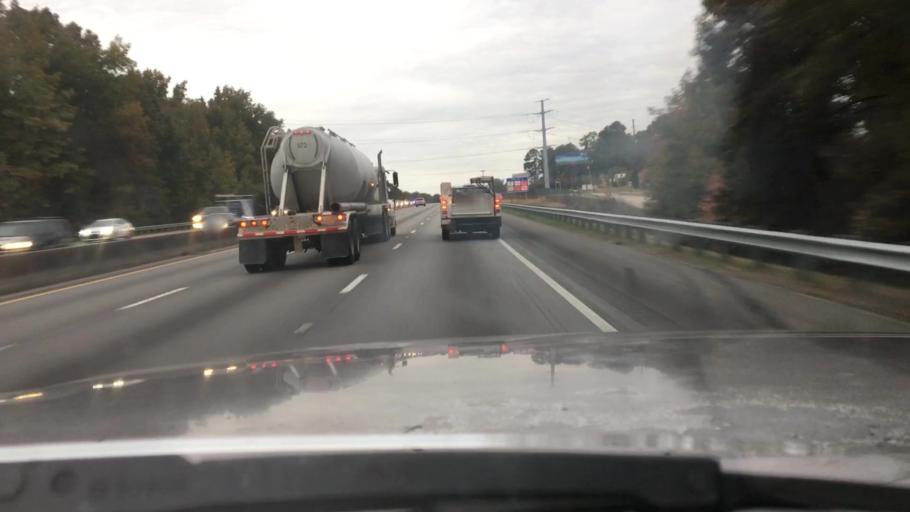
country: US
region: South Carolina
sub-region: Lexington County
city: Saint Andrews
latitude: 34.0203
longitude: -81.1350
